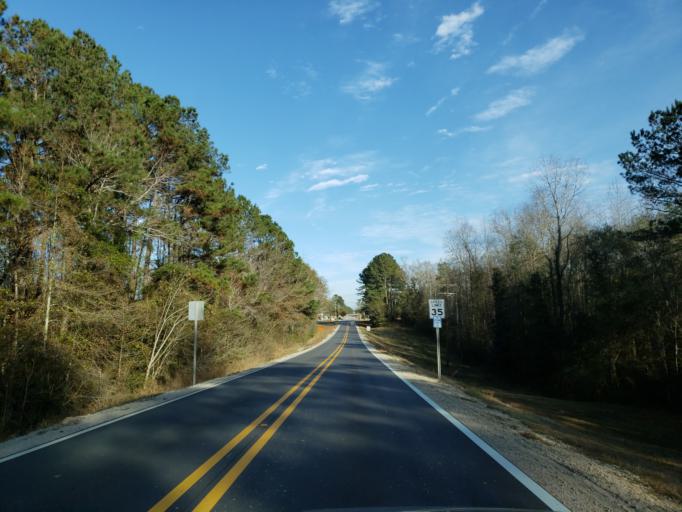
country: US
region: Mississippi
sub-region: Wayne County
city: Belmont
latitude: 31.4334
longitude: -88.4785
